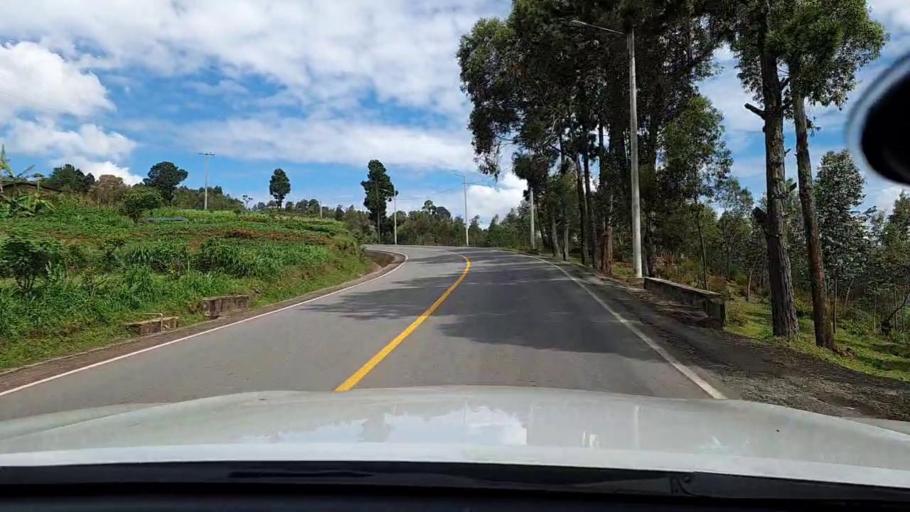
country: RW
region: Kigali
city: Kigali
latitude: -1.8295
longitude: 29.9494
